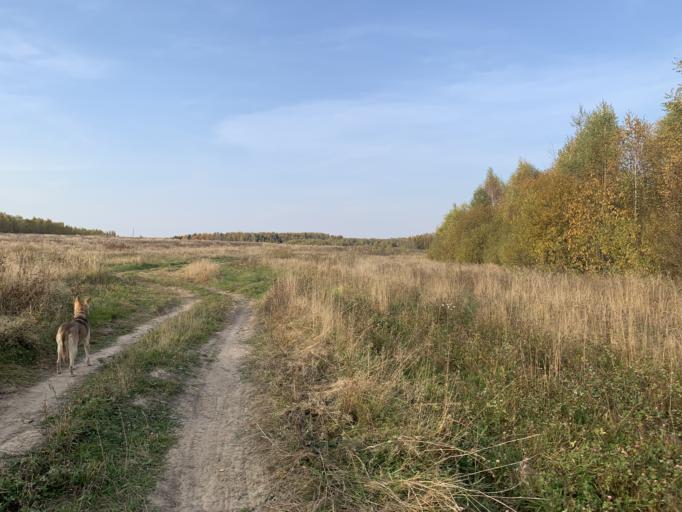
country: RU
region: Jaroslavl
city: Porech'ye-Rybnoye
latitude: 56.9828
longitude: 39.3841
